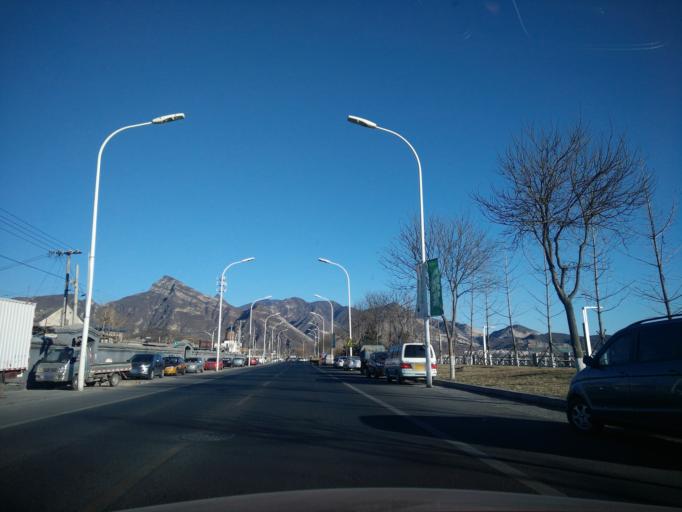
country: CN
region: Beijing
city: Junzhuang
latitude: 39.9831
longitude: 116.0816
